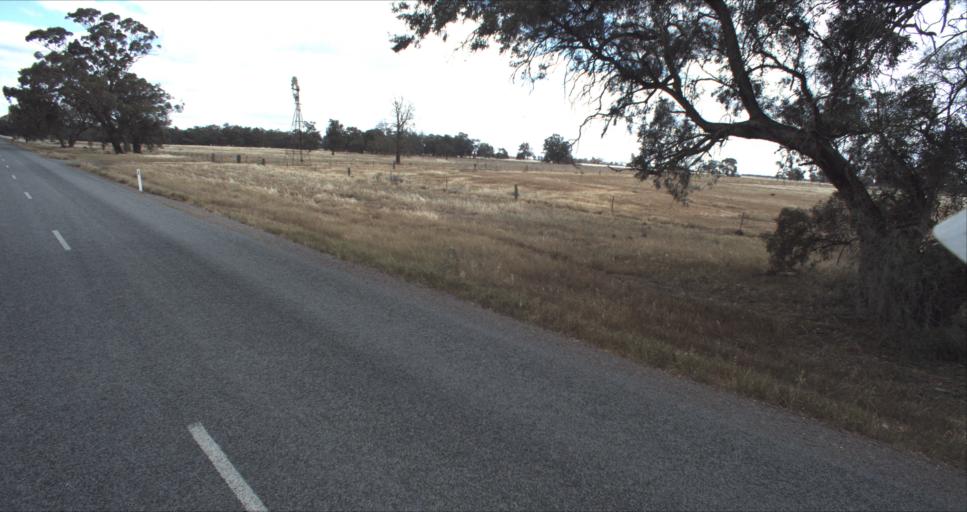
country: AU
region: New South Wales
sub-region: Leeton
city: Leeton
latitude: -34.6858
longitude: 146.3447
